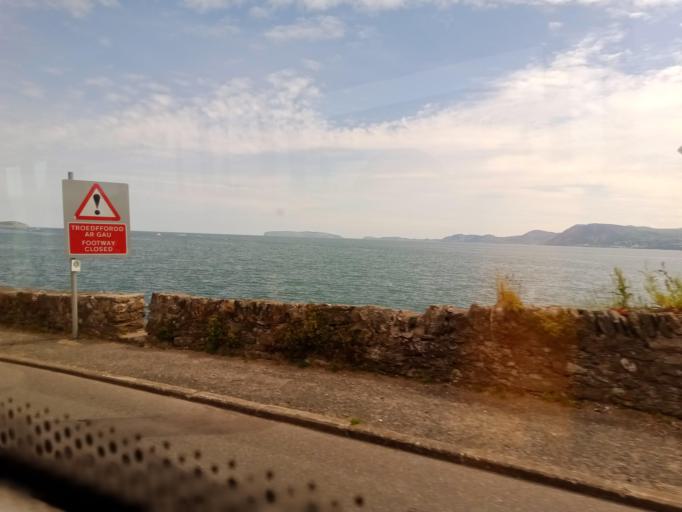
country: GB
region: Wales
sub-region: Anglesey
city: Beaumaris
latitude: 53.2697
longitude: -4.0864
